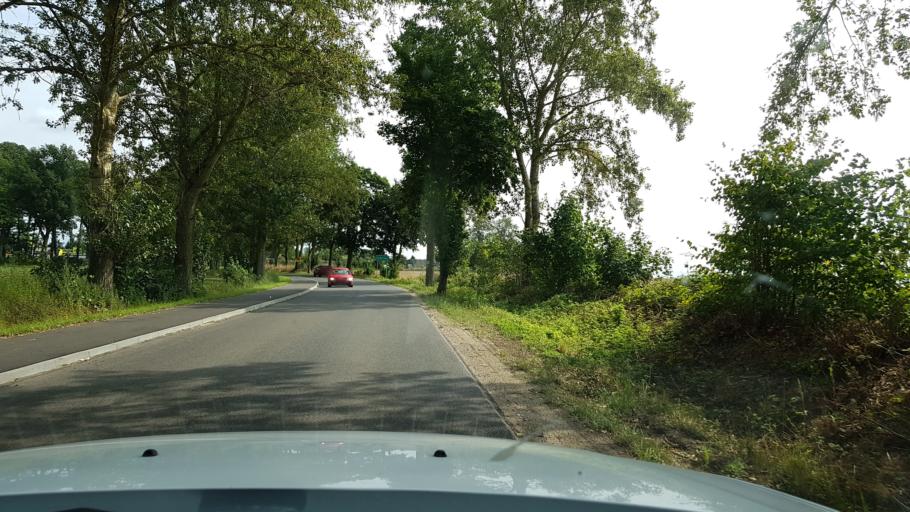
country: PL
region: West Pomeranian Voivodeship
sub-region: Powiat koszalinski
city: Sianow
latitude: 54.2610
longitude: 16.2584
